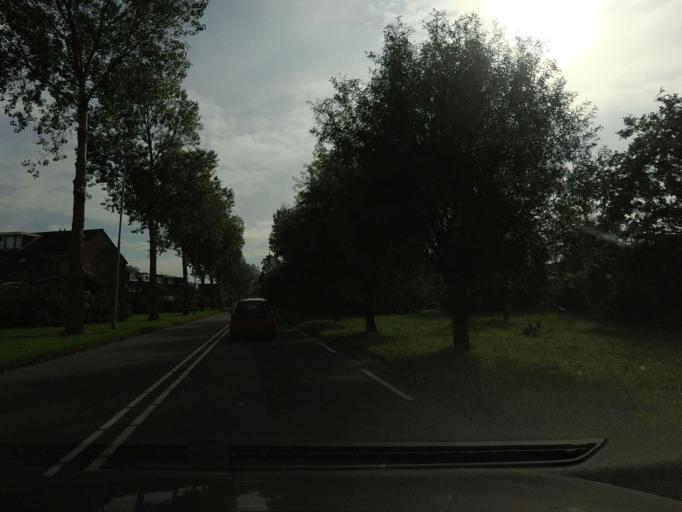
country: NL
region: North Holland
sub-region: Gemeente Den Helder
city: Den Helder
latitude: 52.8908
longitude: 4.7372
